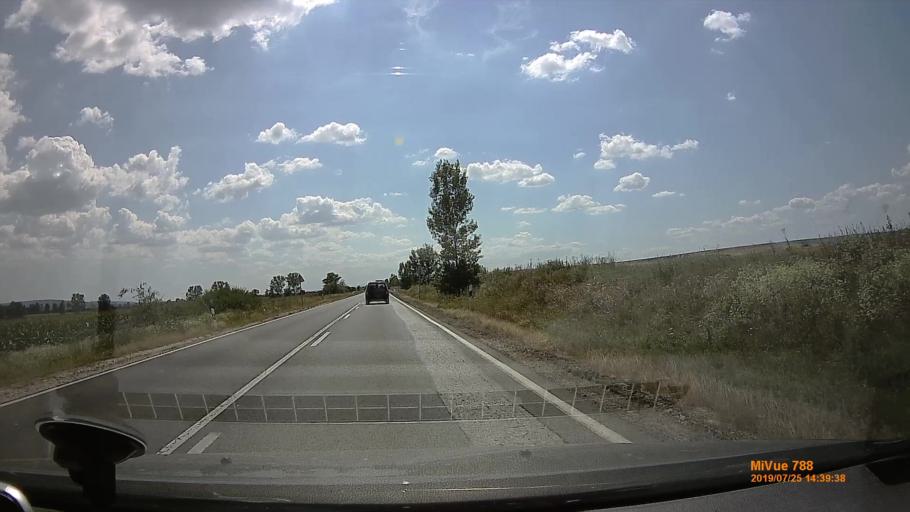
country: HU
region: Borsod-Abauj-Zemplen
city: Halmaj
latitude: 48.2975
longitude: 21.0507
